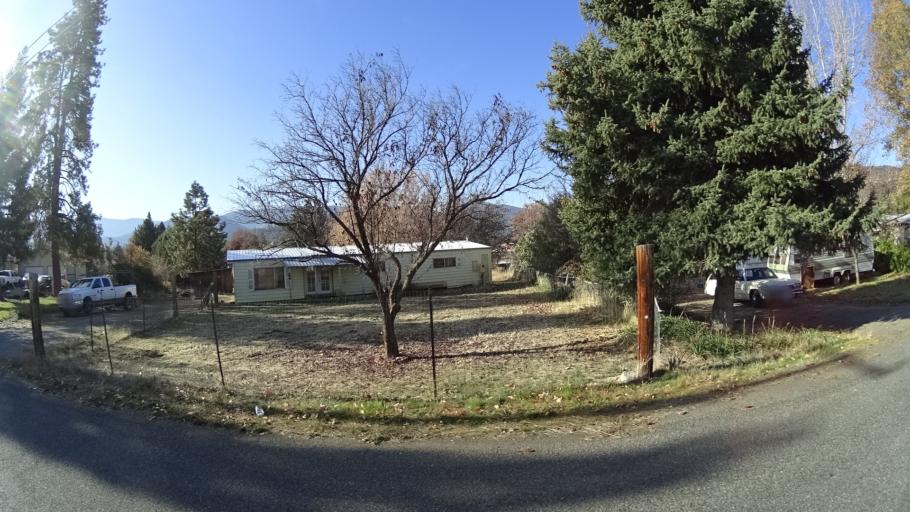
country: US
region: California
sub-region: Siskiyou County
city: Yreka
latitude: 41.6990
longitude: -122.6372
